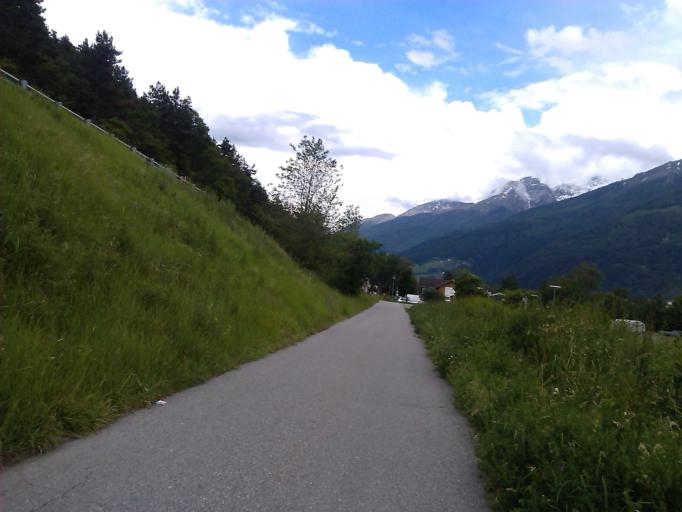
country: IT
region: Trentino-Alto Adige
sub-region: Bolzano
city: Prato Allo Stelvio
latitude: 46.6356
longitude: 10.6082
